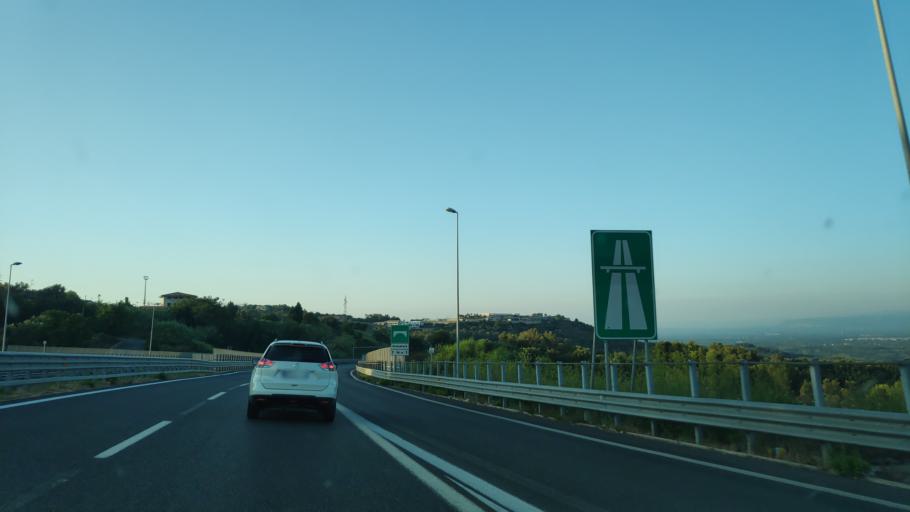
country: IT
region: Calabria
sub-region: Provincia di Reggio Calabria
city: Seminara
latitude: 38.3691
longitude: 15.8660
